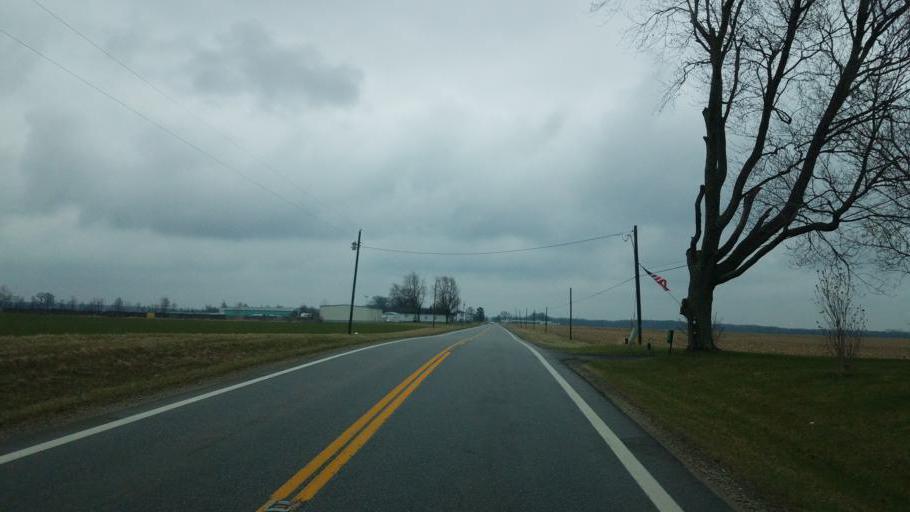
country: US
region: Ohio
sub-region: Delaware County
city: Ashley
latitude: 40.4082
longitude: -82.9349
